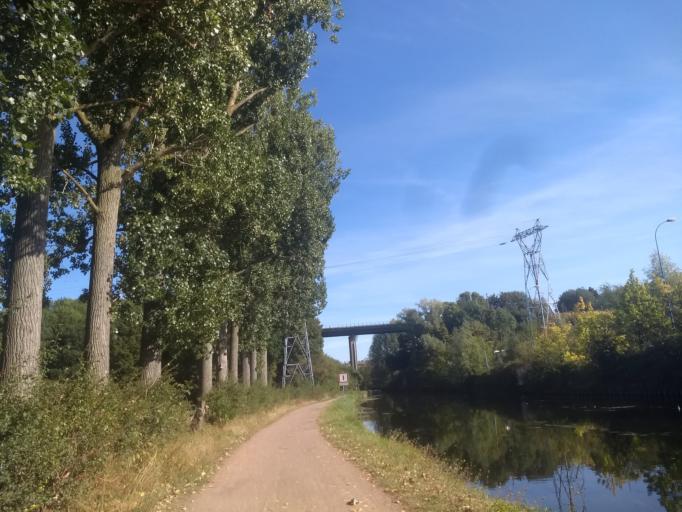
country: FR
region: Nord-Pas-de-Calais
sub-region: Departement du Pas-de-Calais
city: Saint-Laurent-Blangy
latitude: 50.3011
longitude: 2.8206
